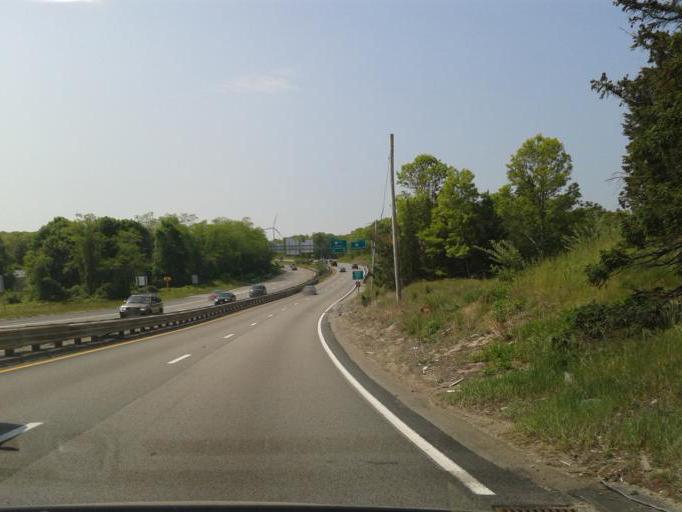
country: US
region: Massachusetts
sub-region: Barnstable County
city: Sagamore
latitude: 41.7722
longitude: -70.5434
